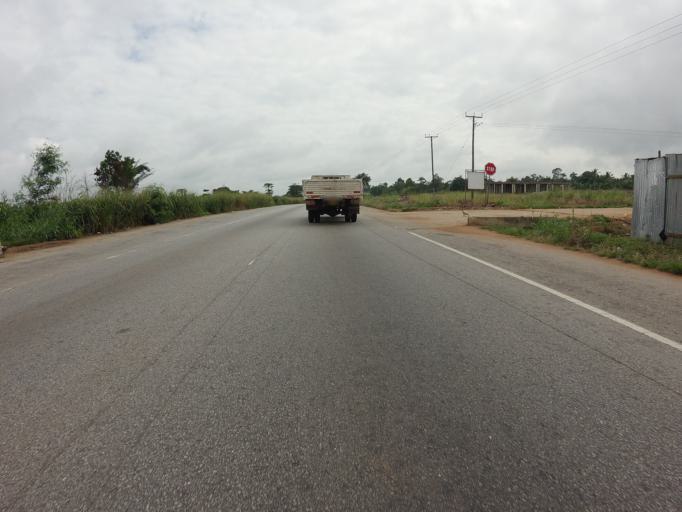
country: GH
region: Ashanti
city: Tafo
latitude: 6.9809
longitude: -1.6874
